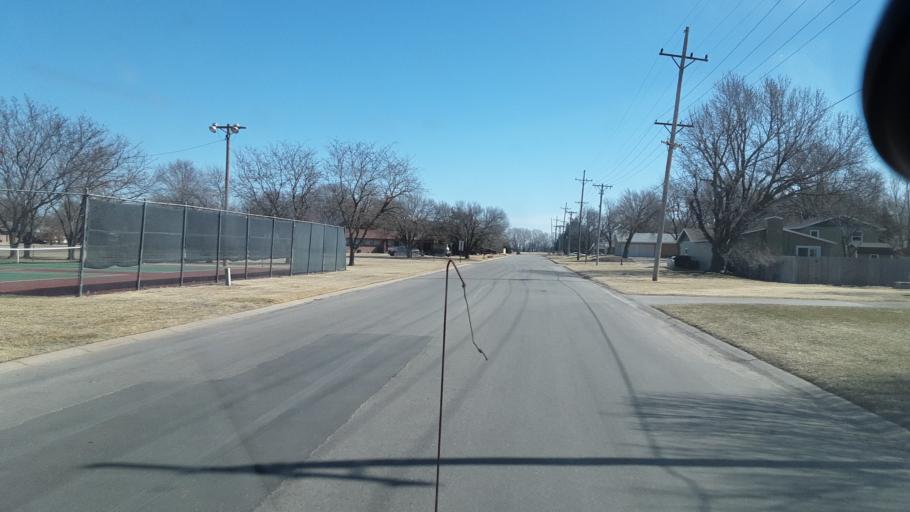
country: US
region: Kansas
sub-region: Rice County
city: Sterling
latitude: 38.2147
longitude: -98.2020
